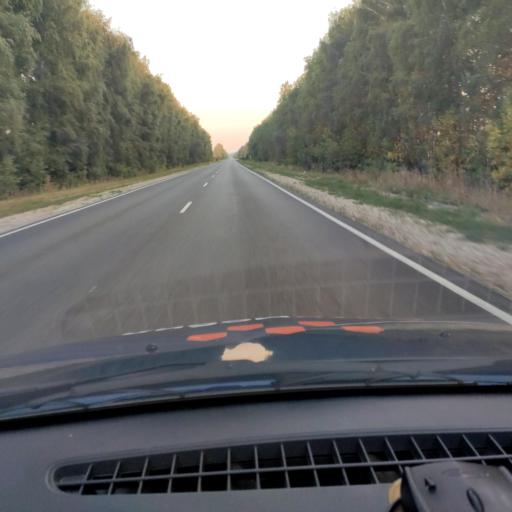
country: RU
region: Voronezj
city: Latnaya
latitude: 51.6404
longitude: 38.7860
